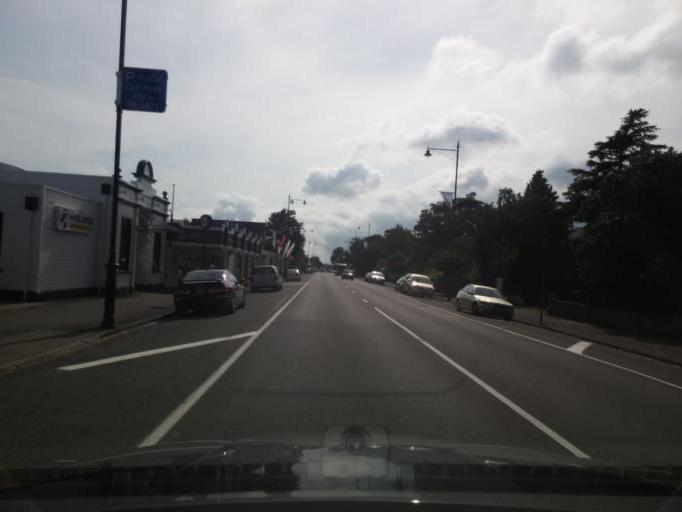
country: NZ
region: Wellington
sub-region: Masterton District
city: Masterton
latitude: -41.0826
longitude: 175.4578
